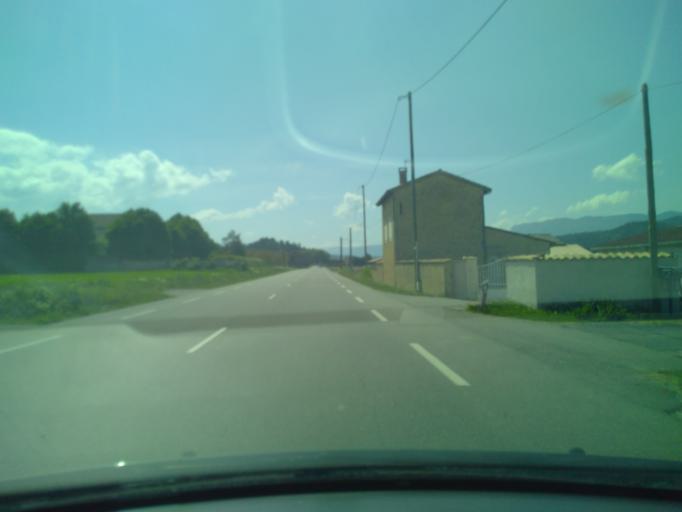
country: FR
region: Rhone-Alpes
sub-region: Departement de la Drome
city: Die
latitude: 44.7352
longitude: 5.3894
